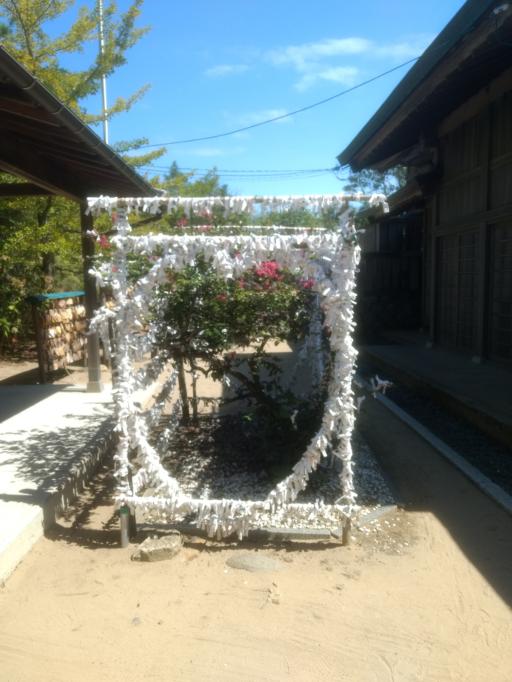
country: JP
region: Tottori
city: Tottori
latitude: 35.5242
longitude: 134.1149
